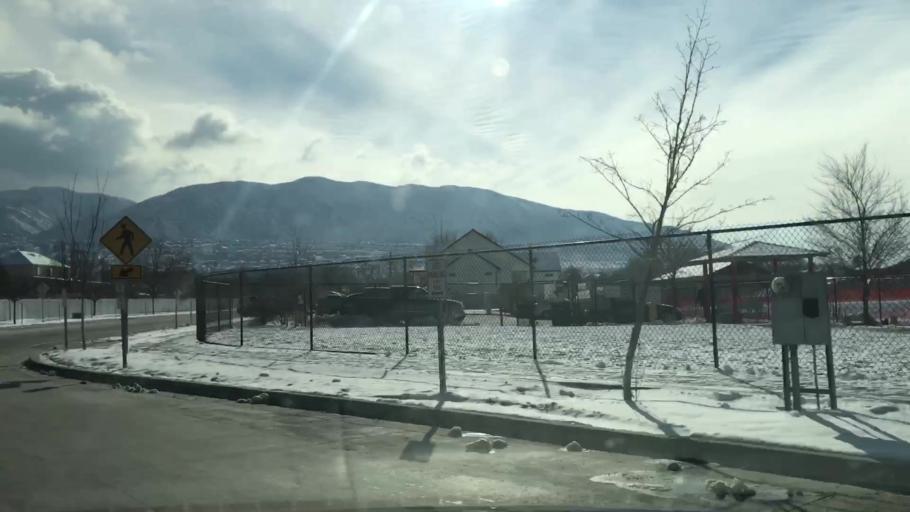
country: US
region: Utah
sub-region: Salt Lake County
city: Draper
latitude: 40.5078
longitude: -111.8821
